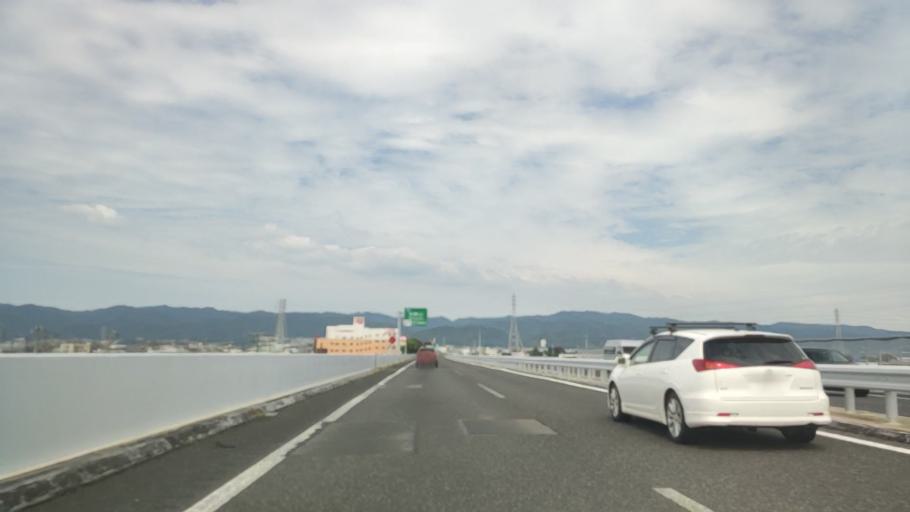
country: JP
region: Wakayama
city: Wakayama-shi
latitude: 34.2346
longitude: 135.2128
